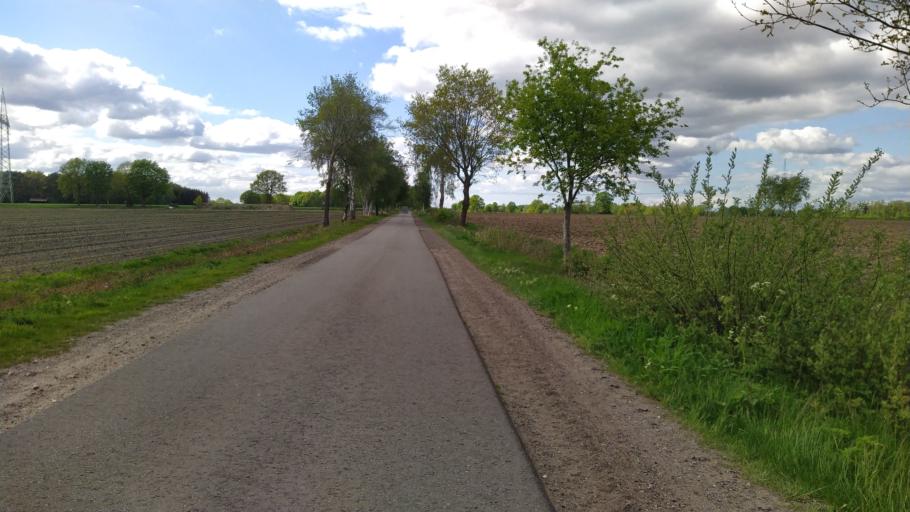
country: DE
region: Lower Saxony
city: Brest
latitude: 53.4423
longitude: 9.4010
